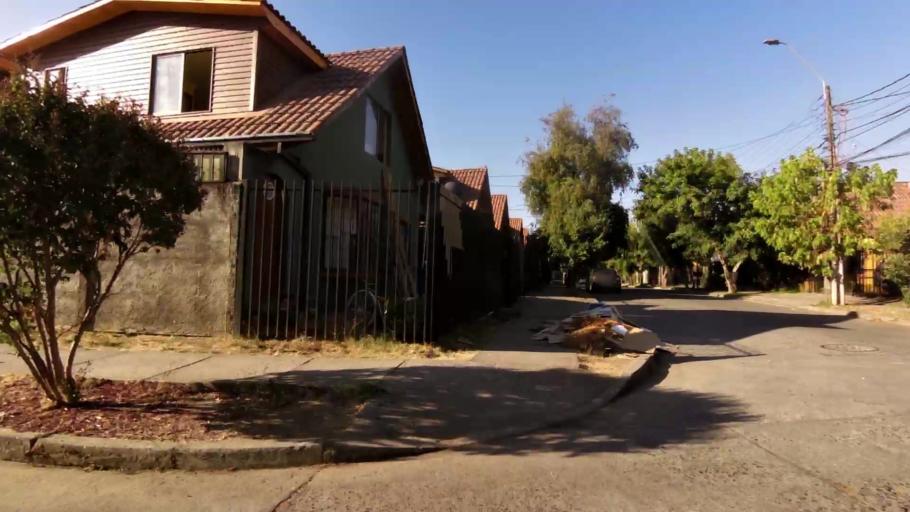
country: CL
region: Maule
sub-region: Provincia de Talca
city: Talca
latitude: -35.4424
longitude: -71.6870
